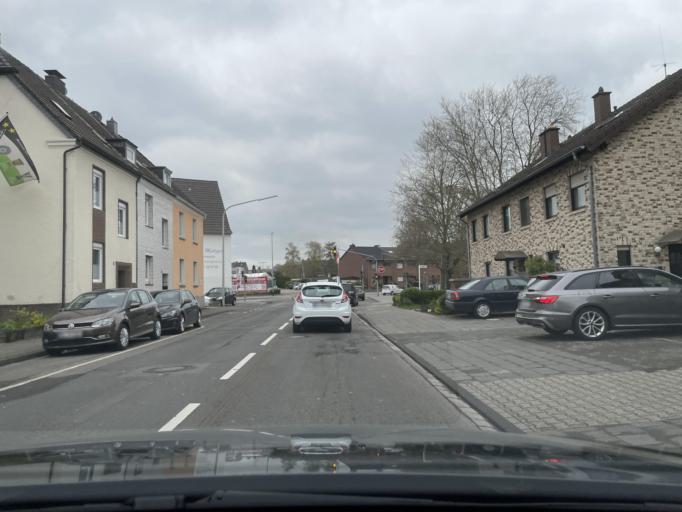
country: DE
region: North Rhine-Westphalia
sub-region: Regierungsbezirk Dusseldorf
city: Monchengladbach
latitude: 51.1666
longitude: 6.4618
